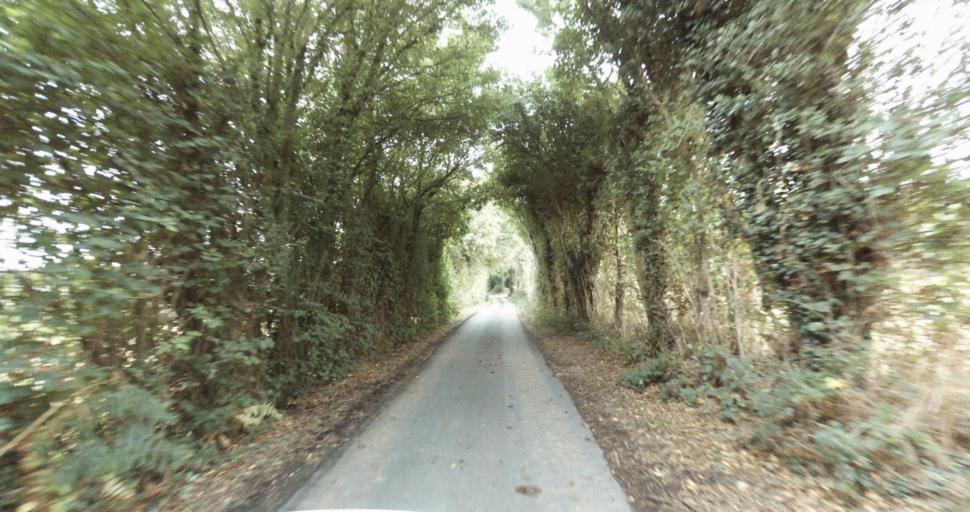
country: FR
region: Lower Normandy
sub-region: Departement de l'Orne
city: Vimoutiers
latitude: 48.9104
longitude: 0.1162
